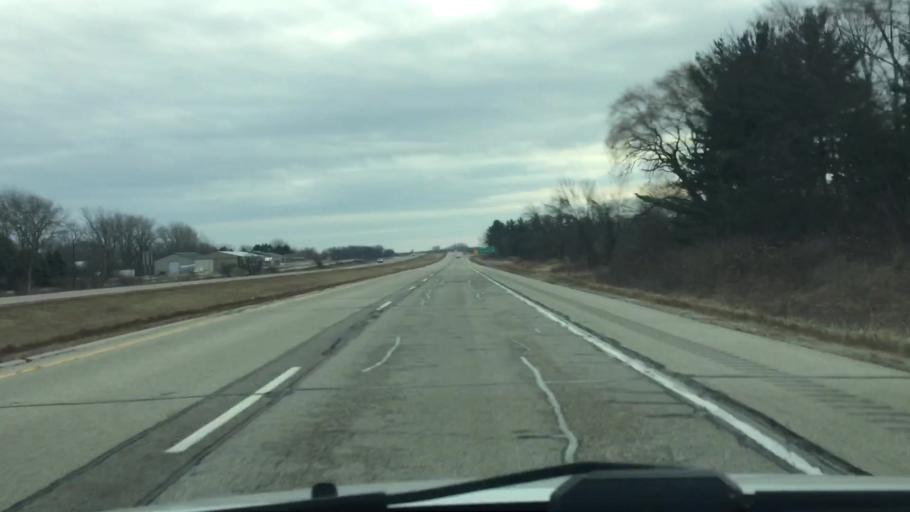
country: US
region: Wisconsin
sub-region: Walworth County
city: Pell Lake
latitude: 42.5509
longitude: -88.3437
